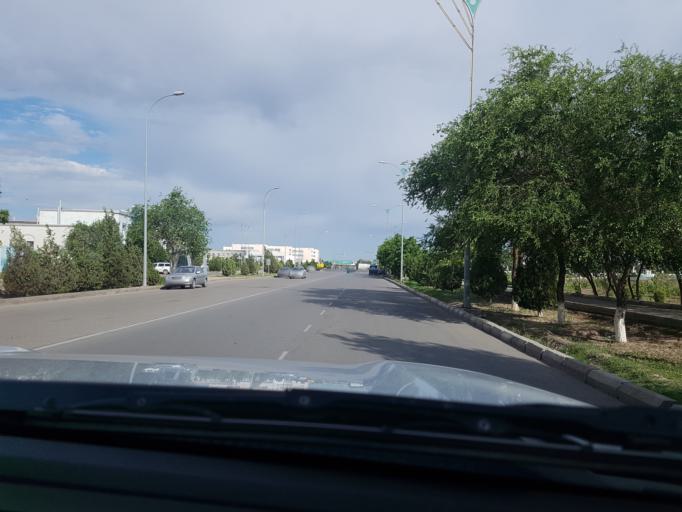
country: TM
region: Dasoguz
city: Dasoguz
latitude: 41.8445
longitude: 59.9342
